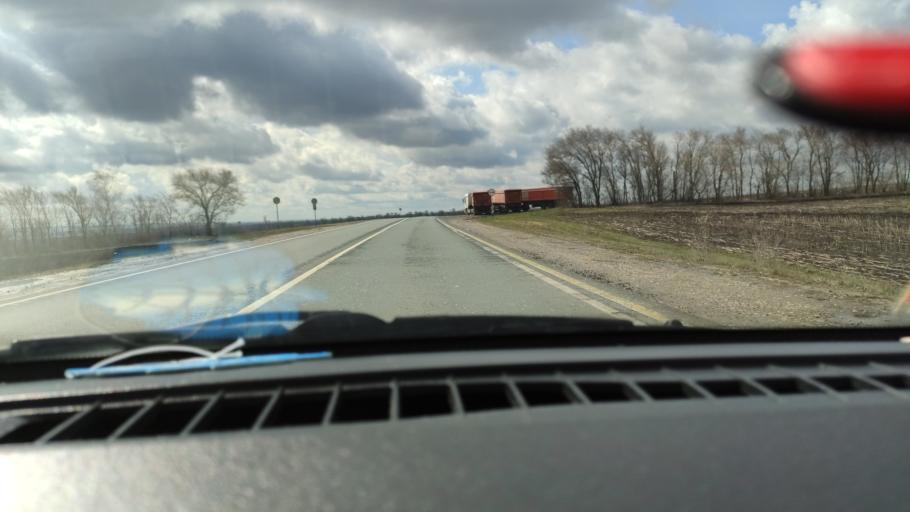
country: RU
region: Samara
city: Yelkhovka
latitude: 53.8633
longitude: 50.2570
